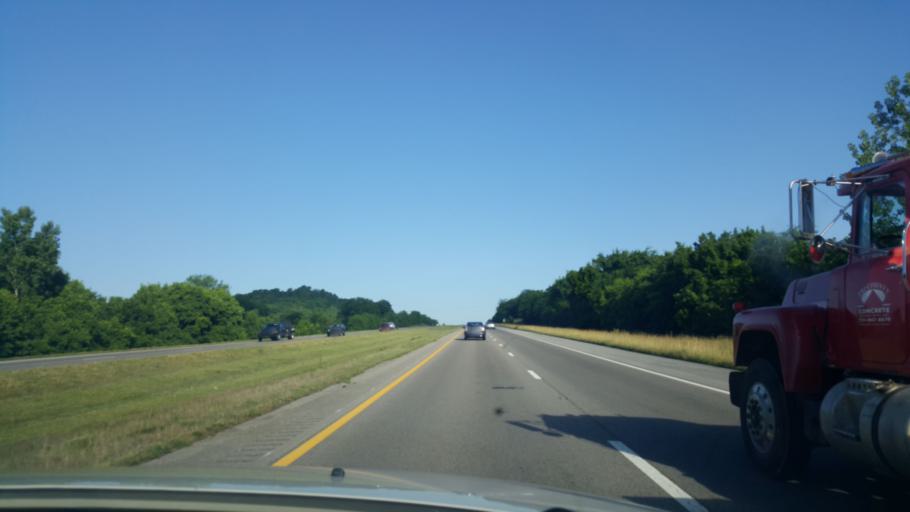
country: US
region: Tennessee
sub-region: Maury County
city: Columbia
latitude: 35.6282
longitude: -87.0874
